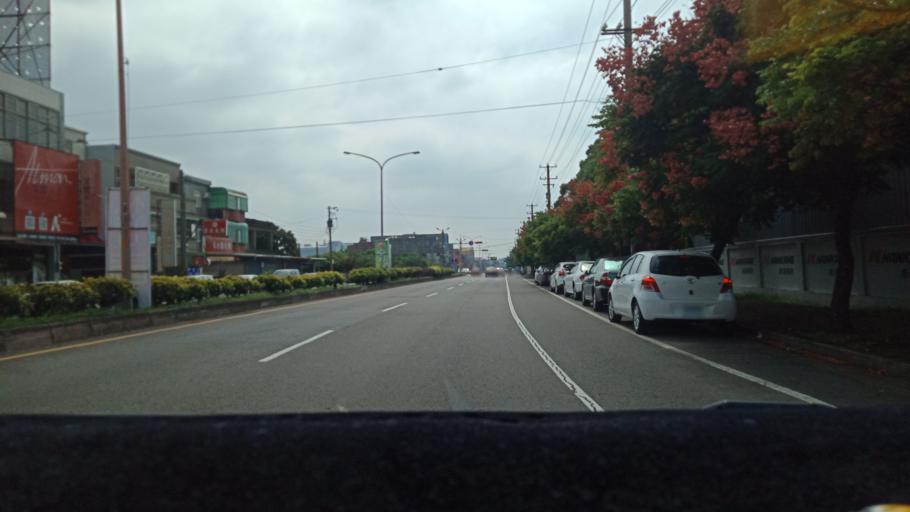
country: TW
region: Taiwan
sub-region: Hsinchu
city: Zhubei
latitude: 24.8769
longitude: 121.0047
